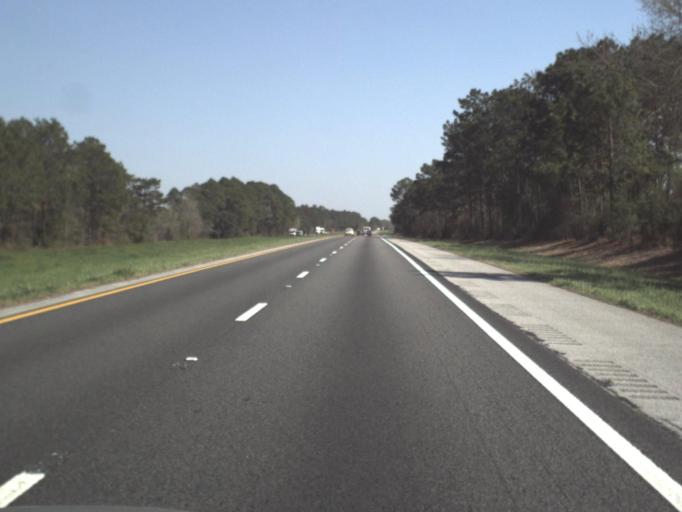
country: US
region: Florida
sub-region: Jackson County
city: Sneads
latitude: 30.6735
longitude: -85.0712
